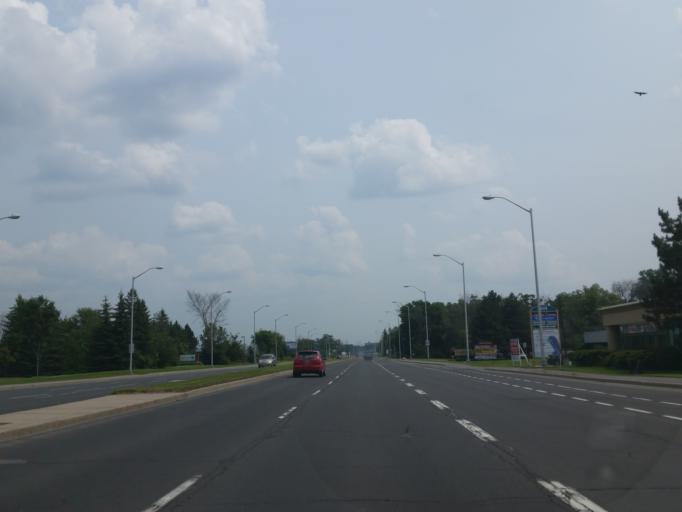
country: CA
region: Ontario
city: Bells Corners
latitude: 45.3480
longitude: -75.9238
